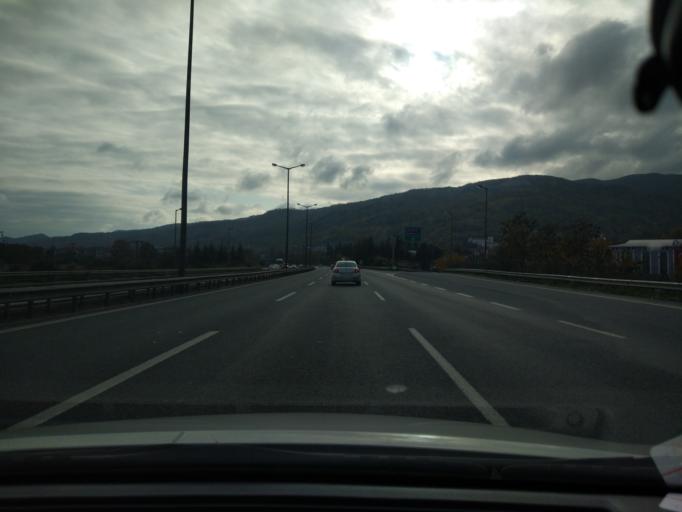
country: TR
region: Sakarya
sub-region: Merkez
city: Sapanca
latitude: 40.6874
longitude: 30.2418
